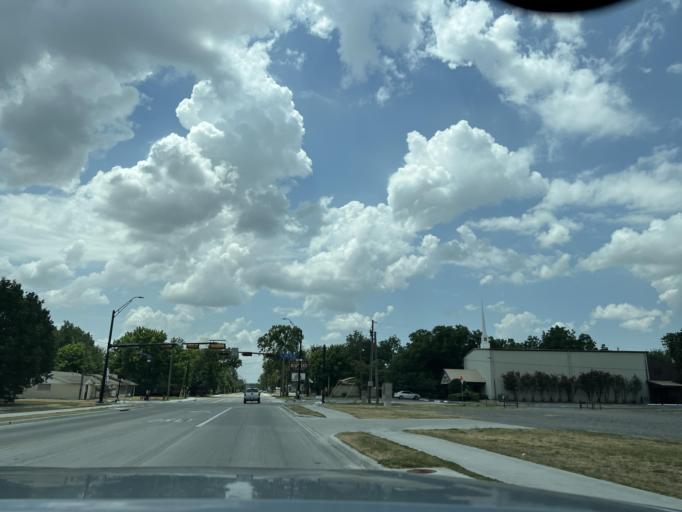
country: US
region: Texas
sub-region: Parker County
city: Springtown
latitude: 32.9713
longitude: -97.6850
